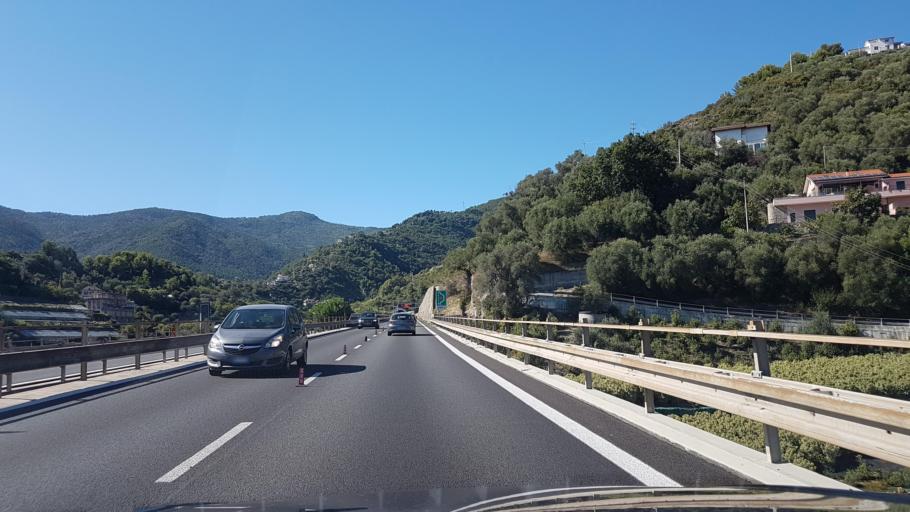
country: IT
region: Liguria
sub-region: Provincia di Imperia
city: San Remo
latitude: 43.8371
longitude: 7.7616
